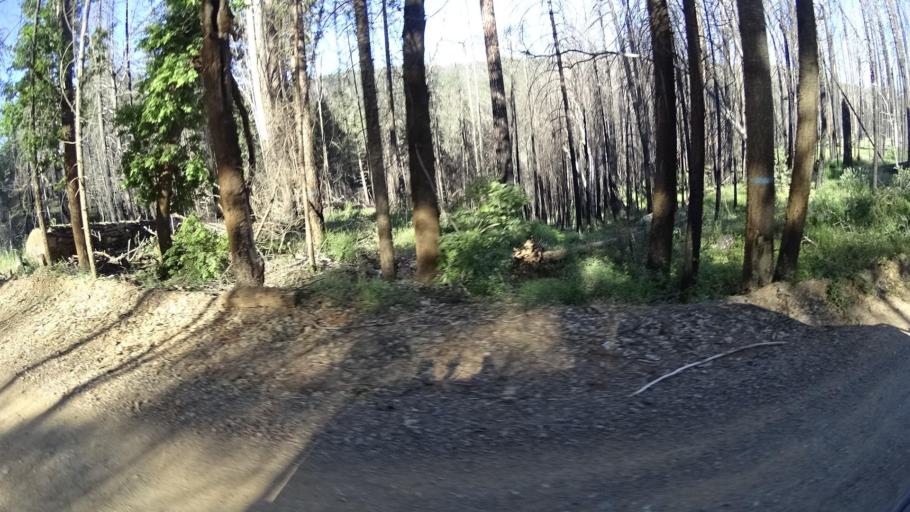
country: US
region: California
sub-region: Lake County
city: Upper Lake
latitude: 39.3685
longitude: -122.9920
